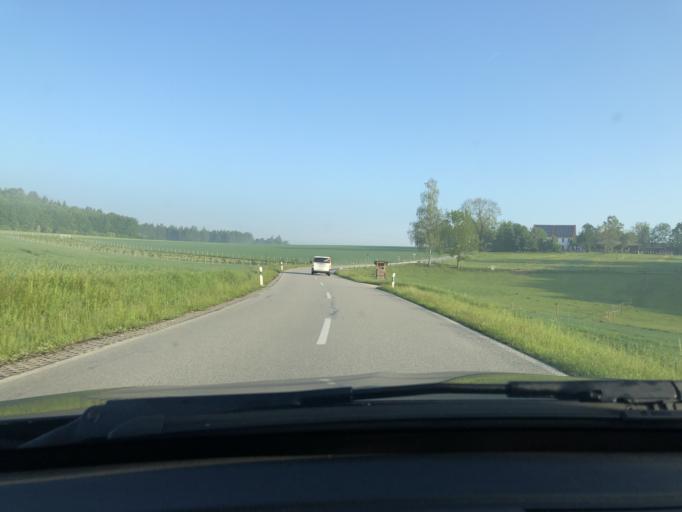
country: DE
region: Bavaria
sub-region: Upper Bavaria
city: Kirchdorf
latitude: 48.4745
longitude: 11.6366
